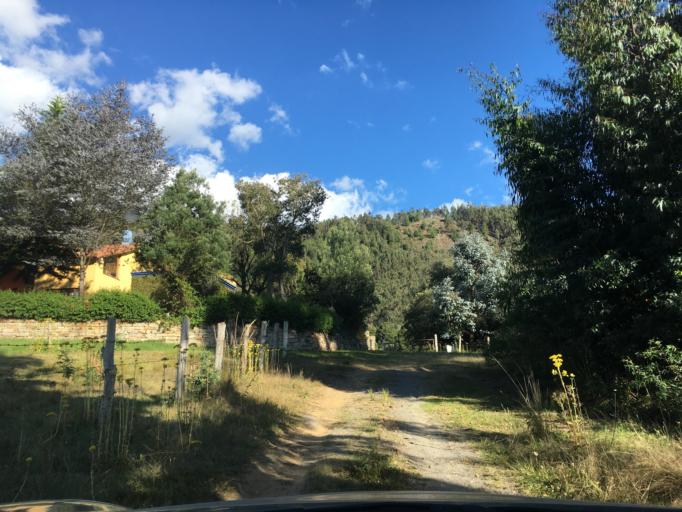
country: CO
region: Boyaca
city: Firavitoba
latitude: 5.6701
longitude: -72.9552
